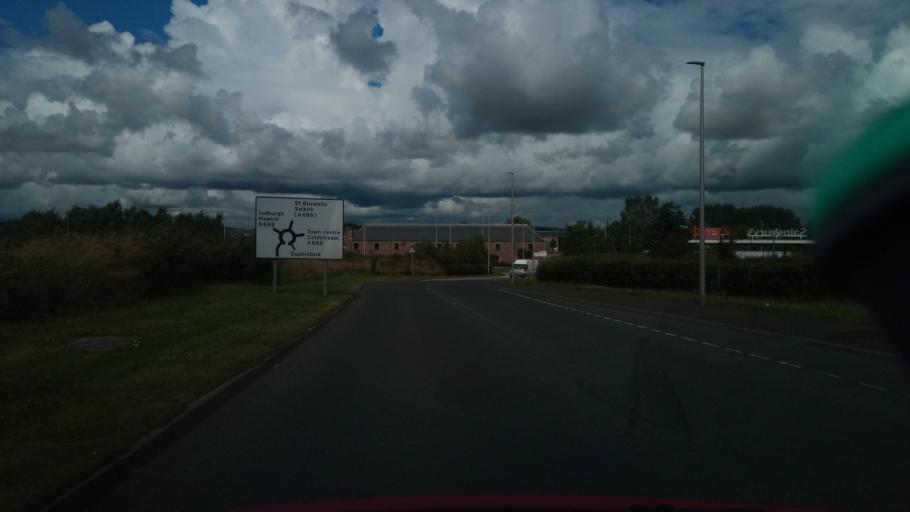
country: GB
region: Scotland
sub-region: The Scottish Borders
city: Kelso
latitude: 55.5893
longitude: -2.4278
